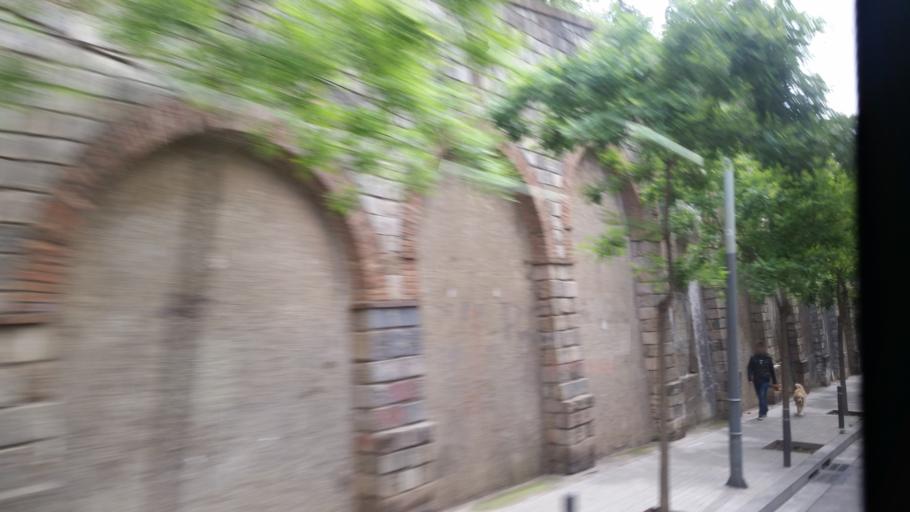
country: ES
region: Catalonia
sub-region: Provincia de Barcelona
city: Horta-Guinardo
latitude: 41.4193
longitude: 2.1588
